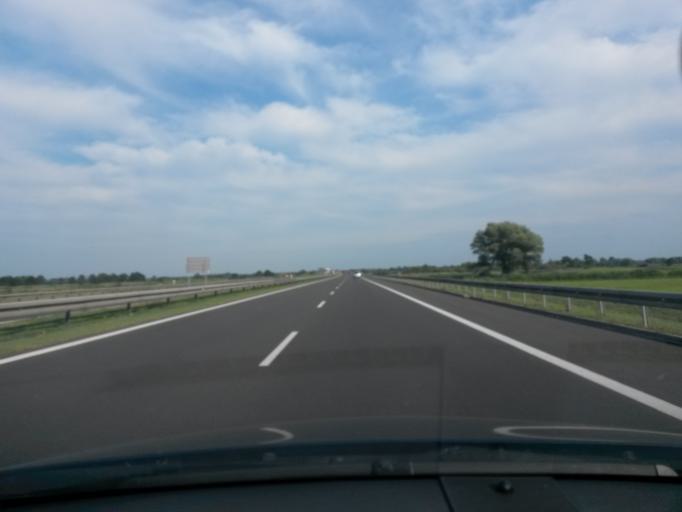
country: PL
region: Greater Poland Voivodeship
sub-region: Powiat koninski
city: Rzgow Pierwszy
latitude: 52.2002
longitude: 18.0365
